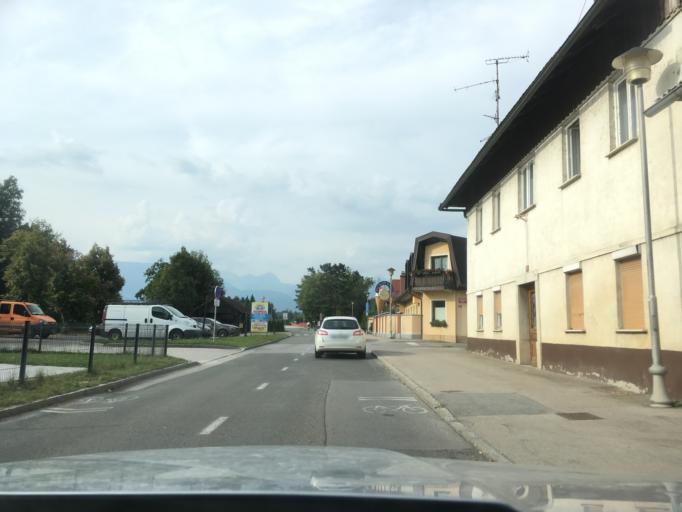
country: SI
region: Domzale
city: Radomlje
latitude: 46.1758
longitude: 14.6103
